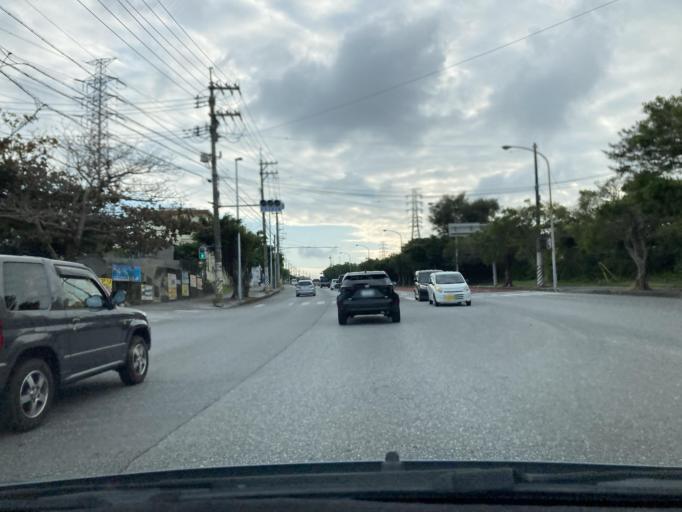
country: JP
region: Okinawa
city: Okinawa
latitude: 26.3521
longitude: 127.8039
